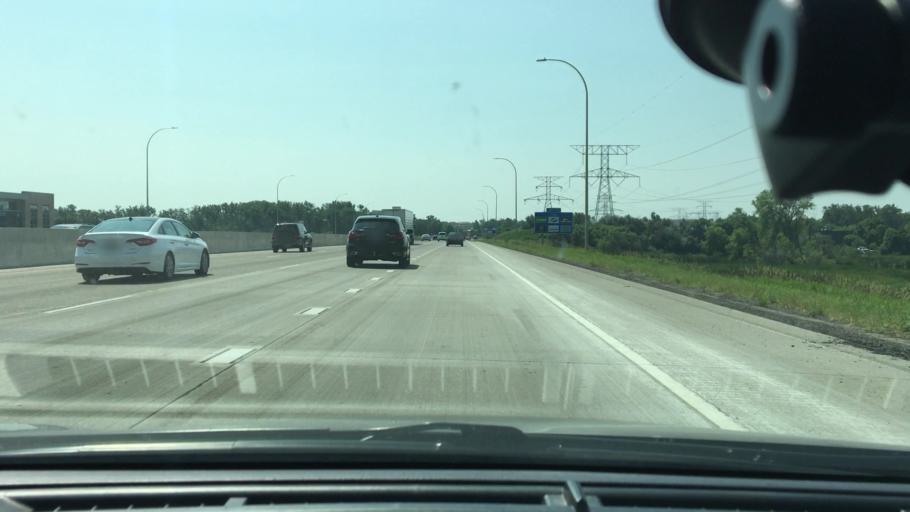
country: US
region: Minnesota
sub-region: Hennepin County
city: Maple Grove
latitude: 45.0774
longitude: -93.4467
